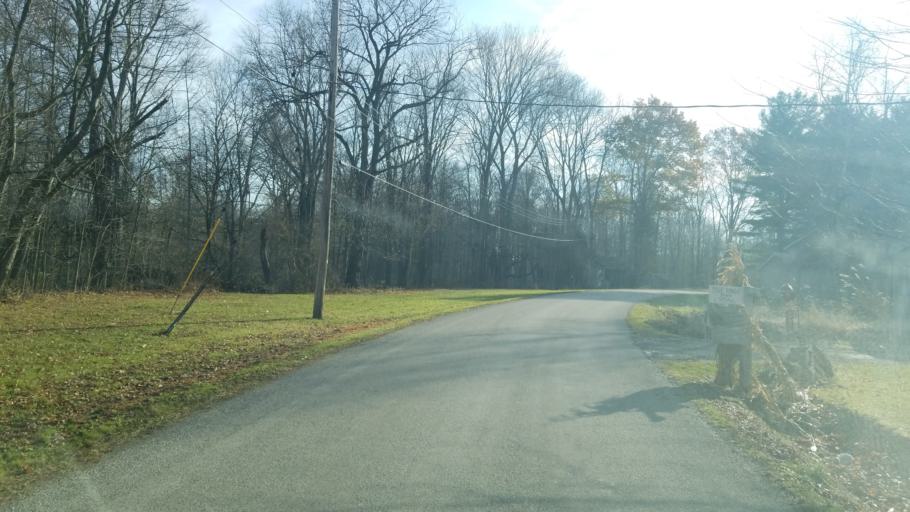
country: US
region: Ohio
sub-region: Ashtabula County
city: North Kingsville
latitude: 41.8475
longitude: -80.6868
